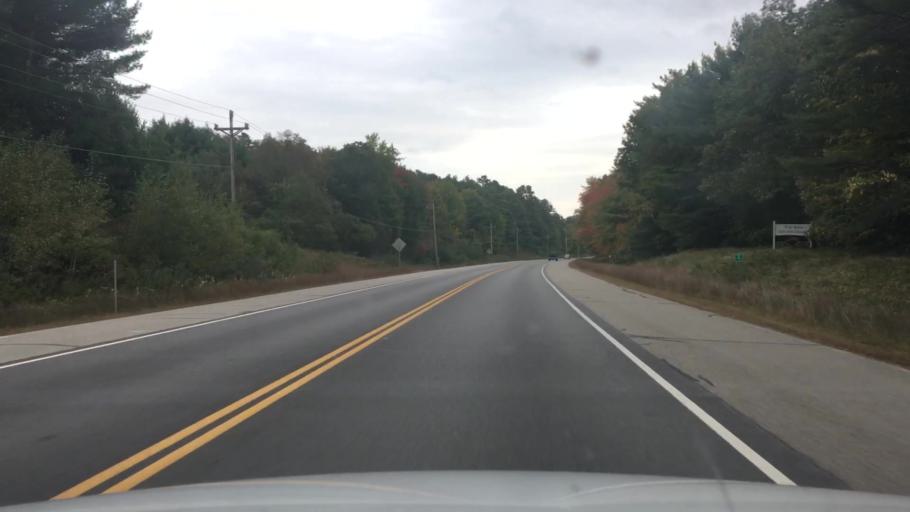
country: US
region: New Hampshire
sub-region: Strafford County
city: New Durham
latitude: 43.4485
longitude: -71.2051
